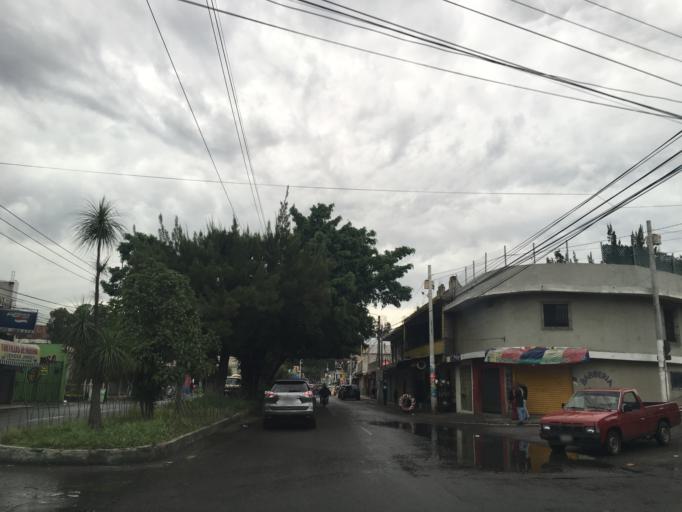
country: GT
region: Guatemala
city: Petapa
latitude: 14.5223
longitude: -90.5472
